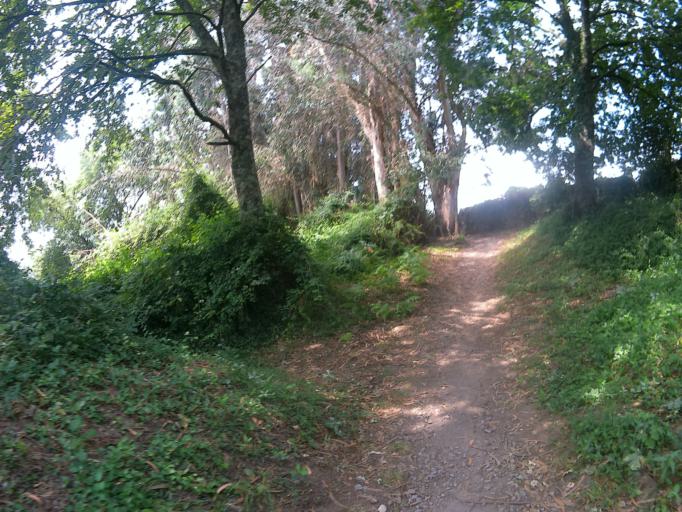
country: PT
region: Viana do Castelo
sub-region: Ponte de Lima
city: Ponte de Lima
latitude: 41.7761
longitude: -8.5842
